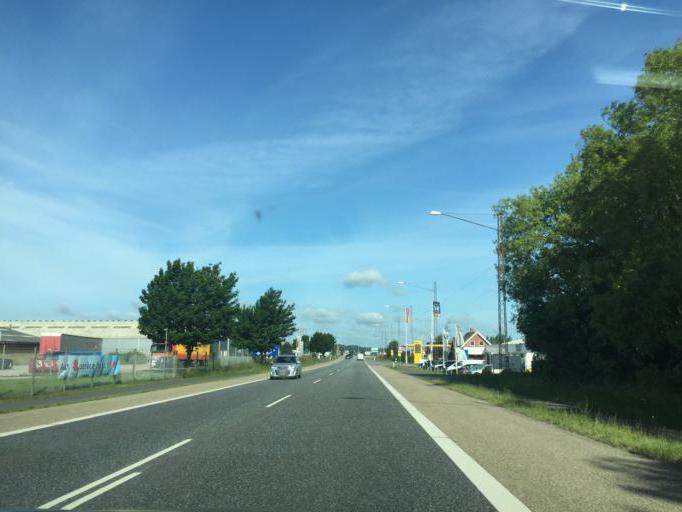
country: DK
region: South Denmark
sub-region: Middelfart Kommune
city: Middelfart
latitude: 55.4960
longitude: 9.7729
